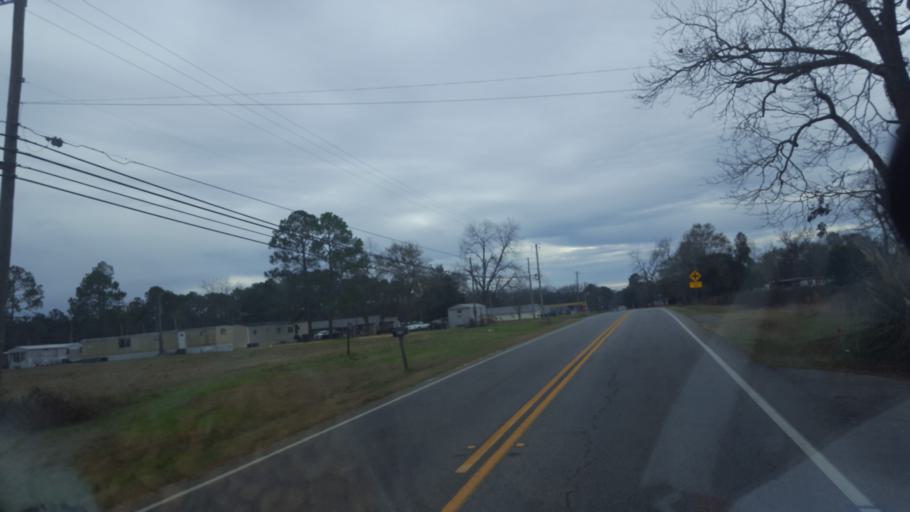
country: US
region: Georgia
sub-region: Ben Hill County
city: Fitzgerald
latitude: 31.7335
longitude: -83.2609
